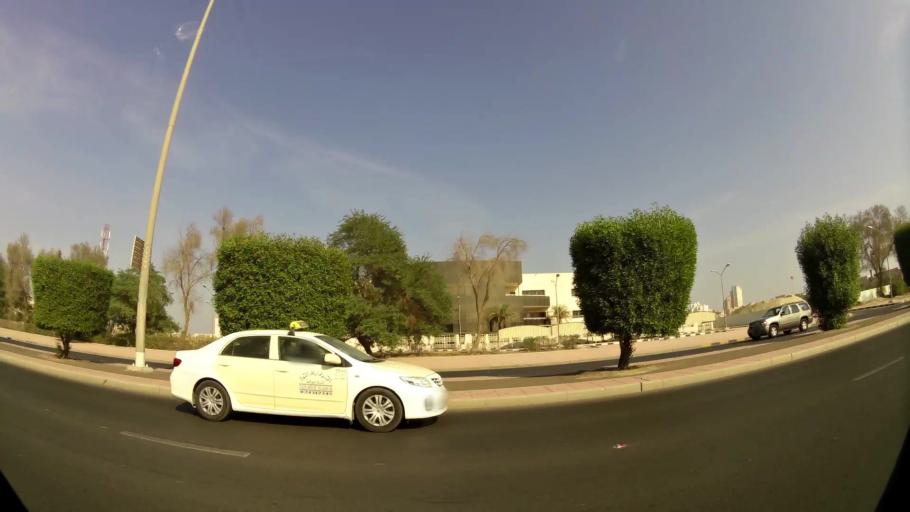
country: KW
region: Al Ahmadi
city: Ar Riqqah
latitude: 29.1626
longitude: 48.1022
